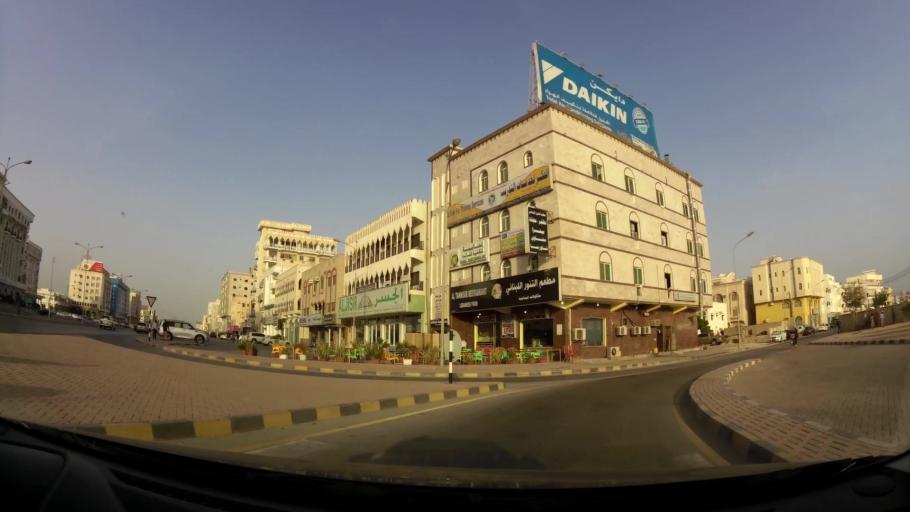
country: OM
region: Zufar
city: Salalah
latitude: 17.0163
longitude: 54.0966
